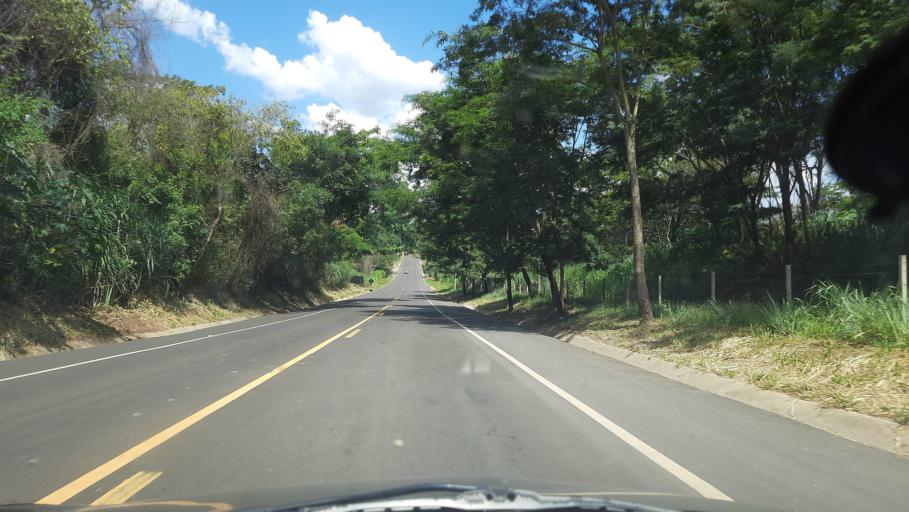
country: BR
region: Sao Paulo
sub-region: Sao Jose Do Rio Pardo
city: Sao Jose do Rio Pardo
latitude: -21.5949
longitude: -46.9870
